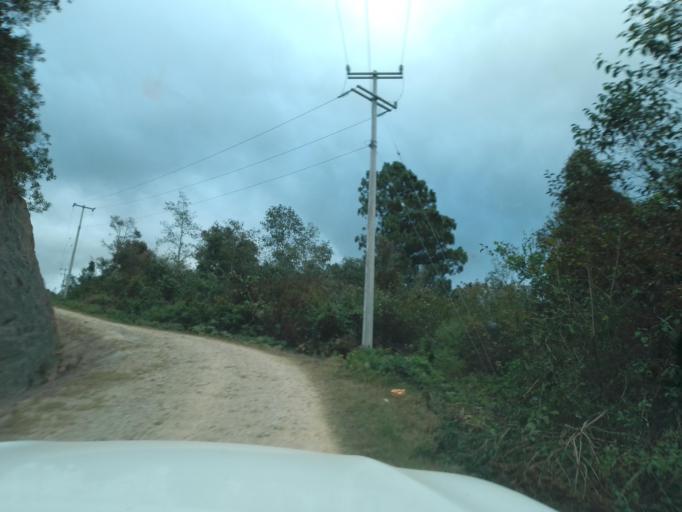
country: MX
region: Chiapas
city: Motozintla de Mendoza
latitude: 15.2133
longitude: -92.2278
